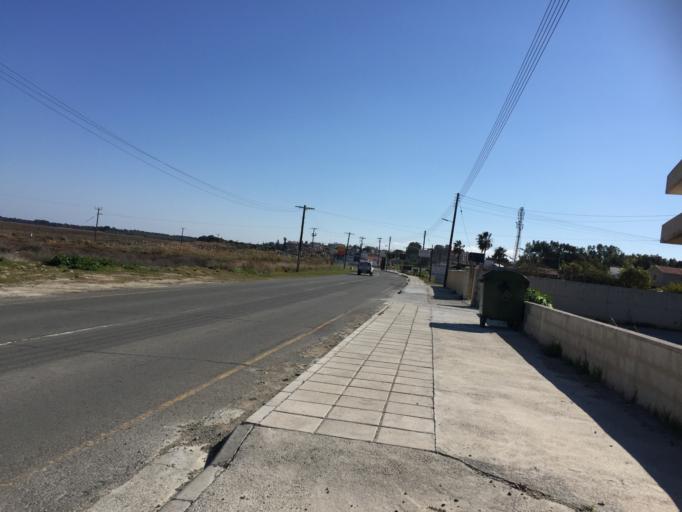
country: CY
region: Larnaka
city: Kolossi
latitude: 34.6056
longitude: 32.9506
